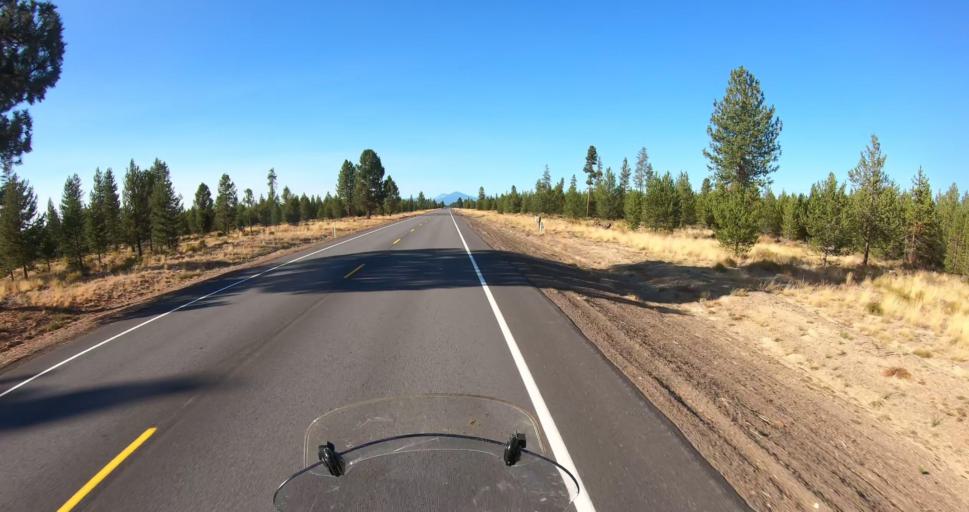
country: US
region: Oregon
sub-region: Deschutes County
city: La Pine
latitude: 43.6183
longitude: -121.5071
